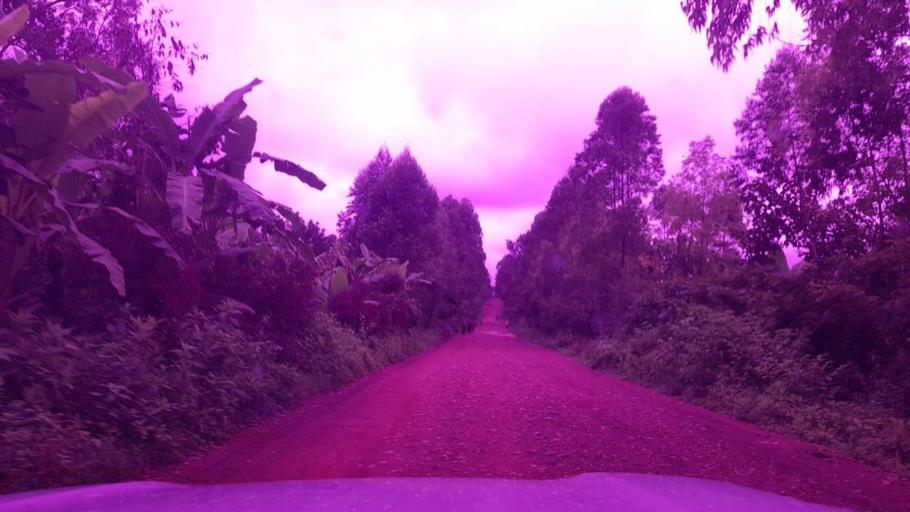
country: ET
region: Southern Nations, Nationalities, and People's Region
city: Bonga
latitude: 7.5809
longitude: 36.0224
